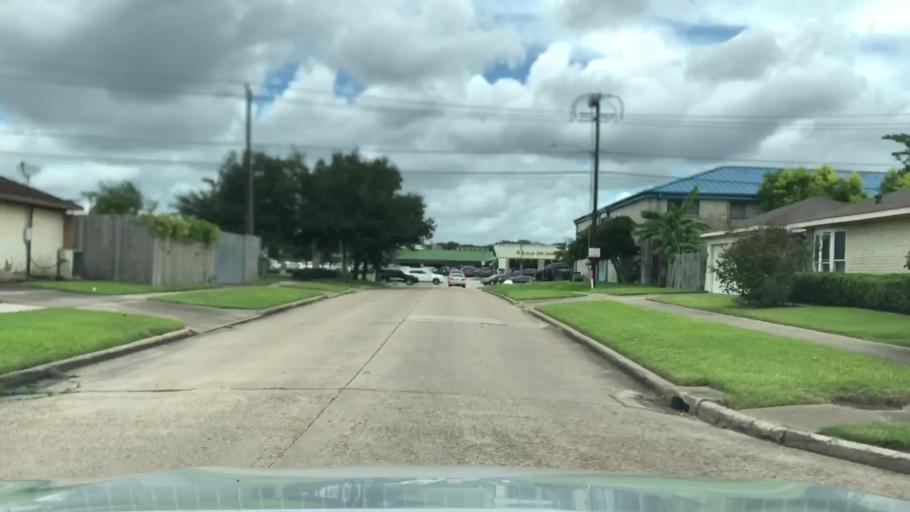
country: US
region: Texas
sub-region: Harris County
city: Piney Point Village
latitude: 29.7039
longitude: -95.5466
